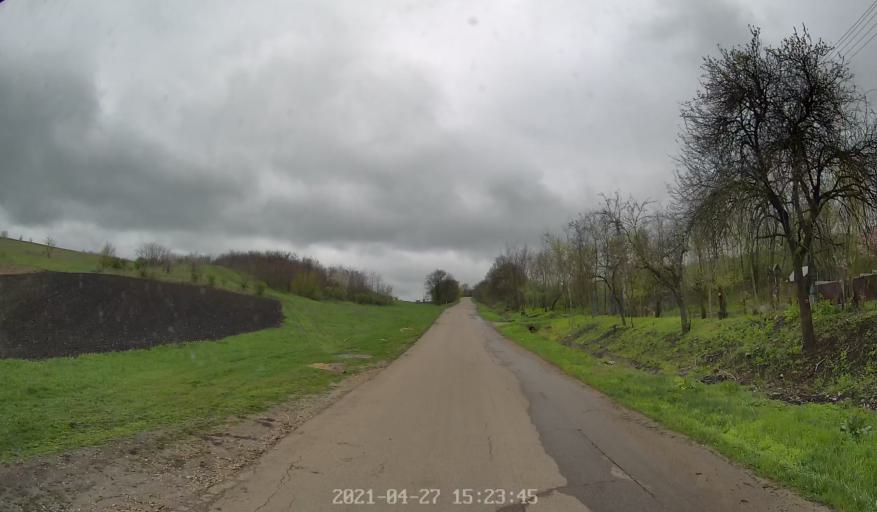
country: MD
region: Chisinau
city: Vadul lui Voda
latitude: 47.0191
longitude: 29.0249
